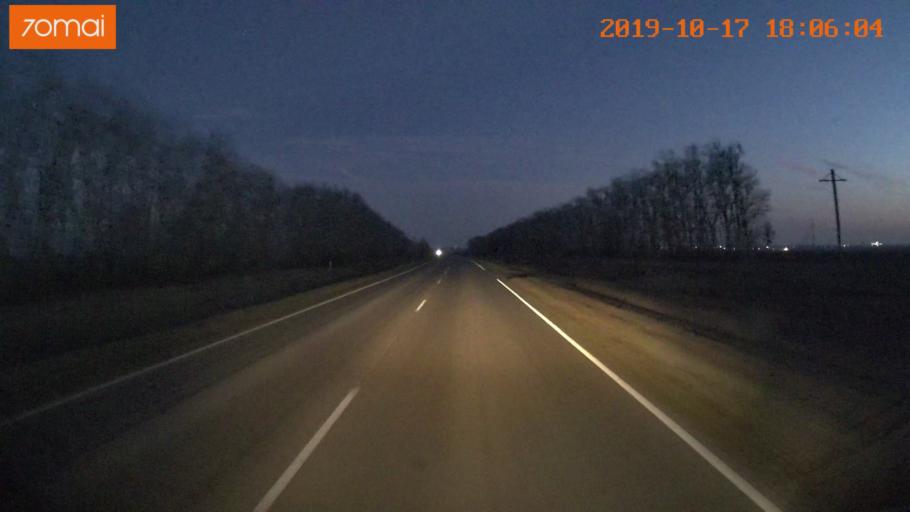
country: RU
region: Tula
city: Kurkino
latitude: 53.4569
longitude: 38.6512
